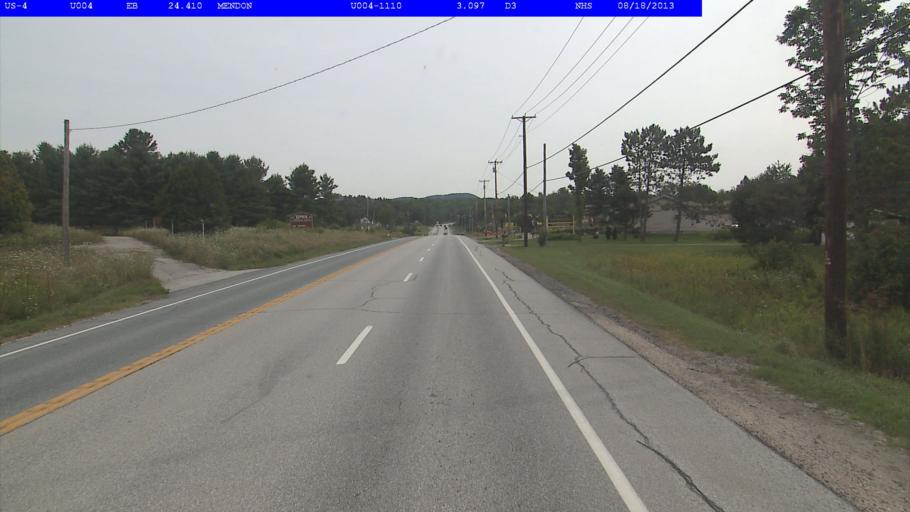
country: US
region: Vermont
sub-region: Rutland County
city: Rutland
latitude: 43.6514
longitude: -72.8938
